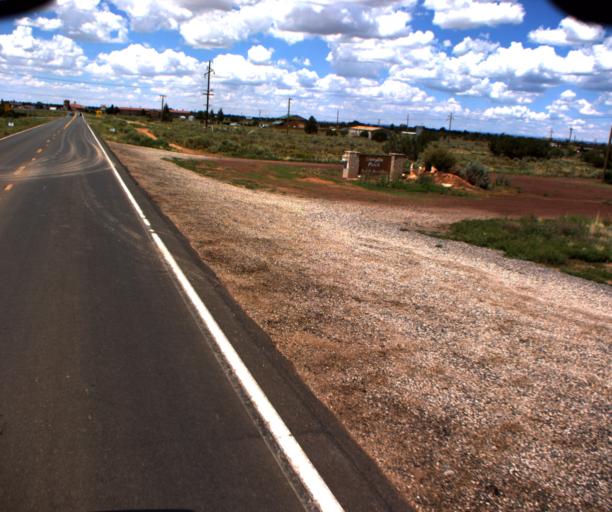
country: US
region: Arizona
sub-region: Coconino County
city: Grand Canyon Village
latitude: 35.6483
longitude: -112.1342
